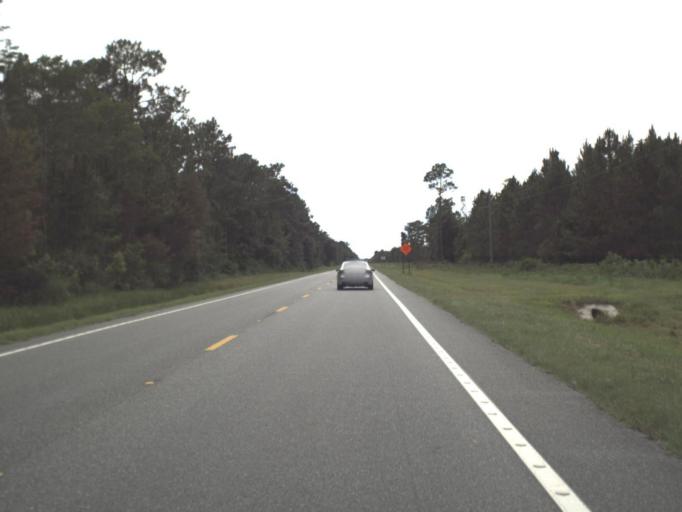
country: US
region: Florida
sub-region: Taylor County
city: Perry
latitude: 30.1010
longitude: -83.4482
